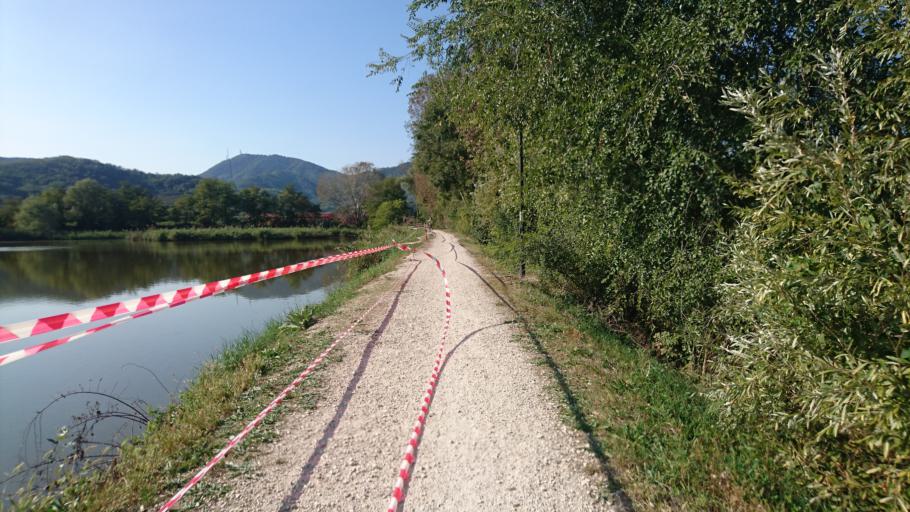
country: IT
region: Veneto
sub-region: Provincia di Padova
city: Galzignano
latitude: 45.3022
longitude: 11.7495
